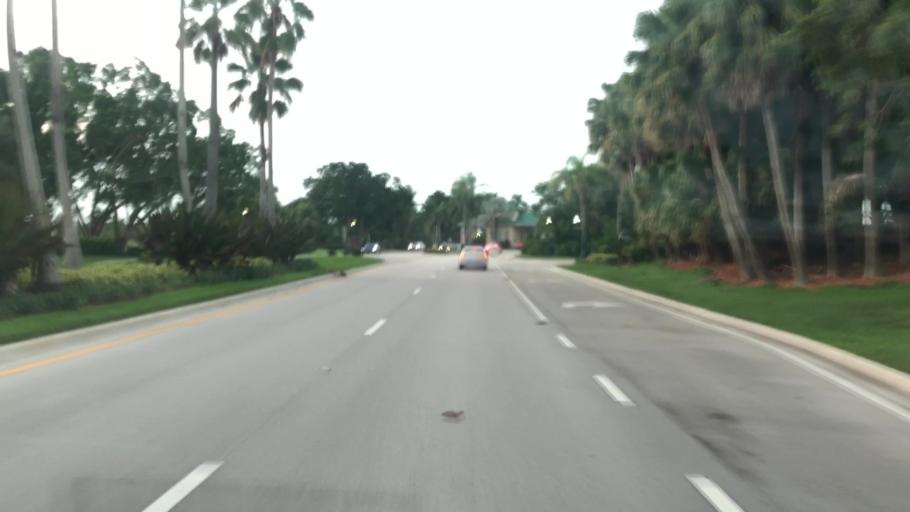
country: US
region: Florida
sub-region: Broward County
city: Weston
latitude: 26.0902
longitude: -80.3919
